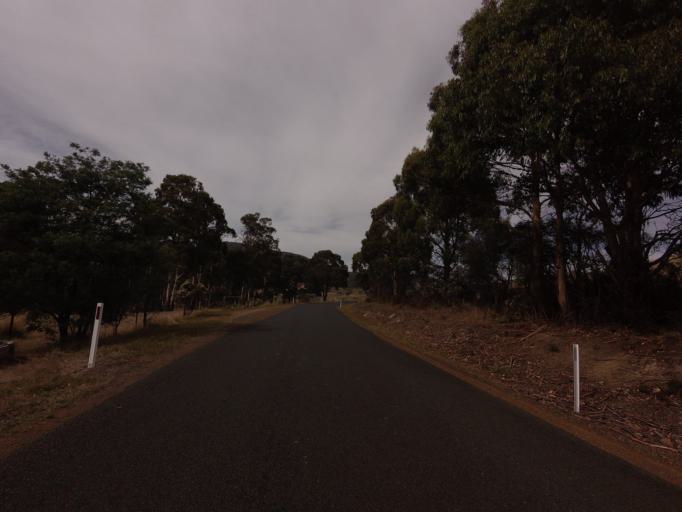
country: AU
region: Tasmania
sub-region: Sorell
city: Sorell
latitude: -42.4746
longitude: 147.5740
